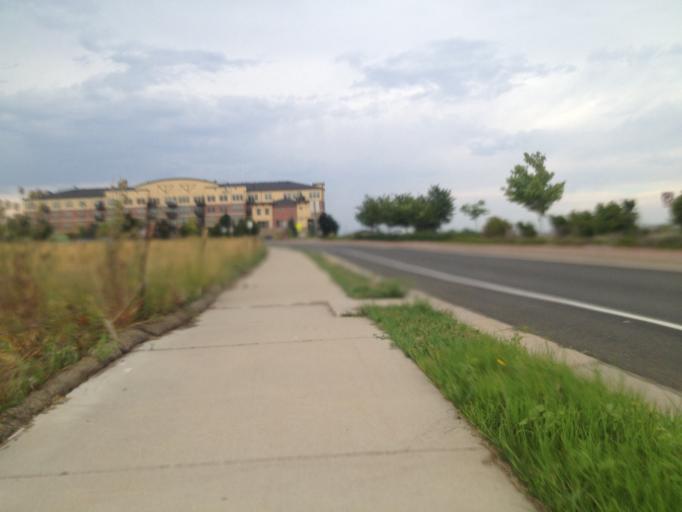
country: US
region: Colorado
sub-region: Boulder County
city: Louisville
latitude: 39.9392
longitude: -105.1243
